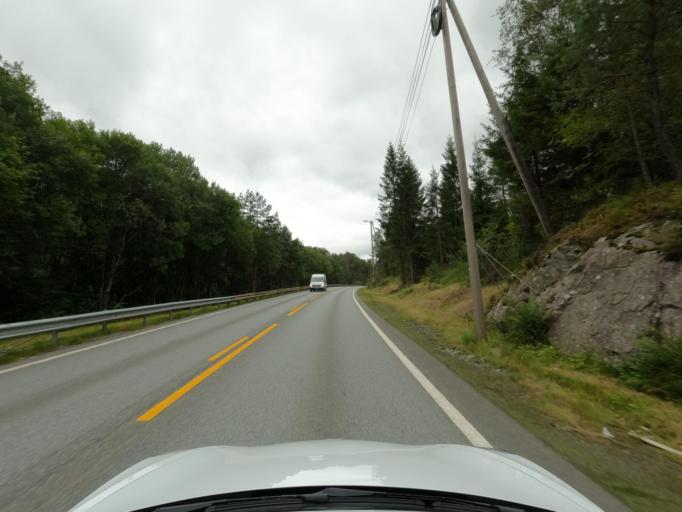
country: NO
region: Hordaland
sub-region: Bergen
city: Indre Arna
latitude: 60.4053
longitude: 5.4692
